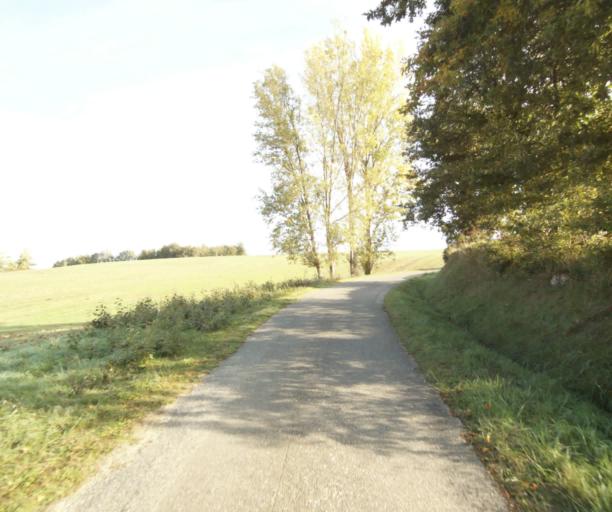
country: FR
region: Midi-Pyrenees
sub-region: Departement de la Haute-Garonne
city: Villemur-sur-Tarn
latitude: 43.9108
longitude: 1.5051
